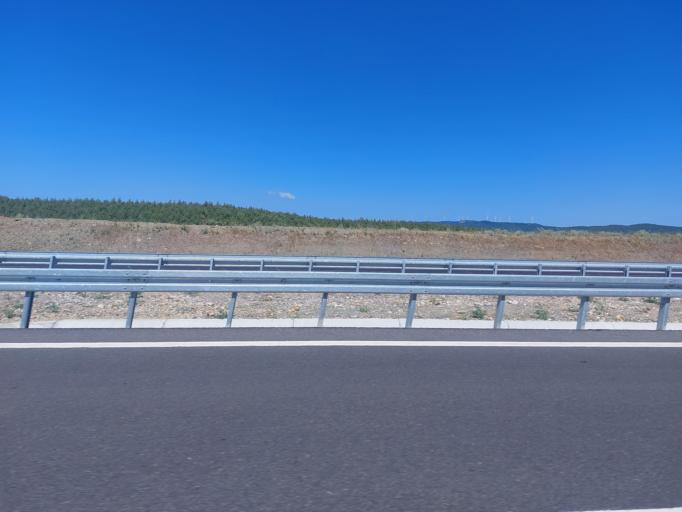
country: TR
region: Canakkale
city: Evrese
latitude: 40.7282
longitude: 26.9886
